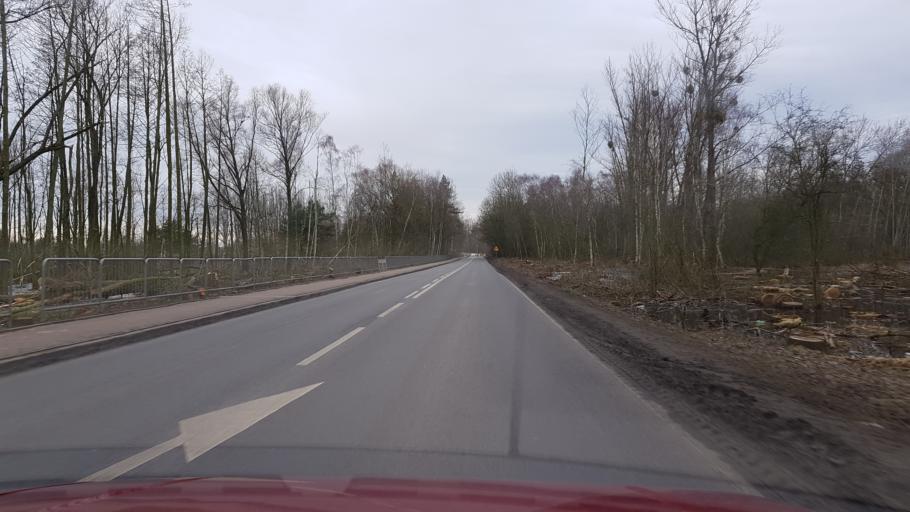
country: PL
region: West Pomeranian Voivodeship
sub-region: Powiat policki
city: Police
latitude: 53.5645
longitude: 14.5602
